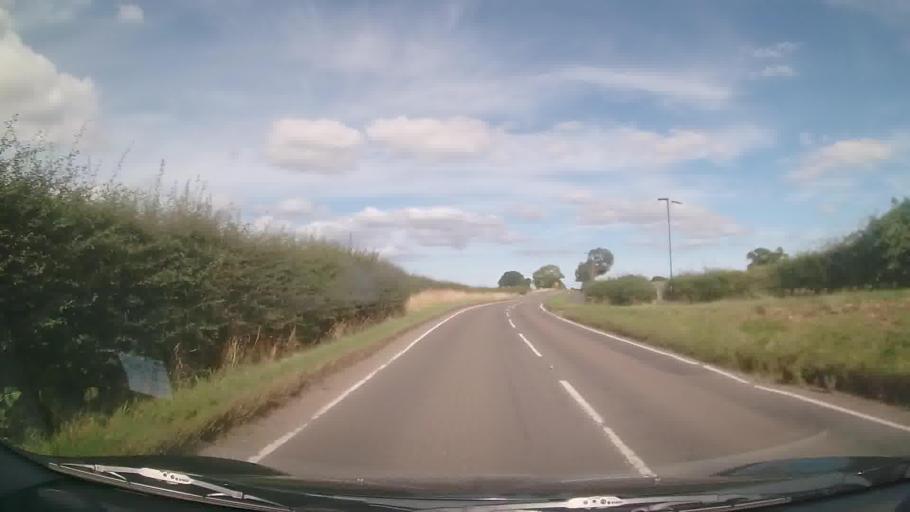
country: GB
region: England
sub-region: Shropshire
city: Pontesbury
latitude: 52.6454
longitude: -2.9122
